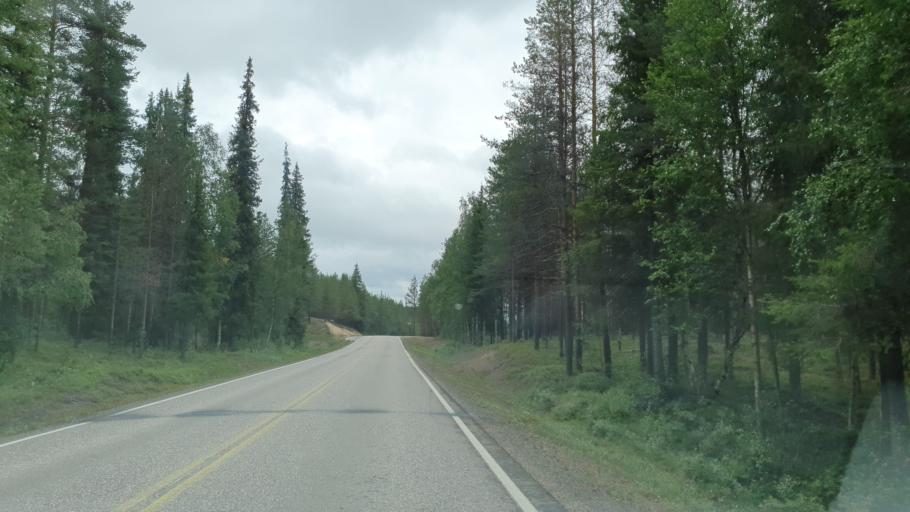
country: FI
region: Lapland
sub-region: Tunturi-Lappi
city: Kolari
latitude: 67.5586
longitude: 24.0156
